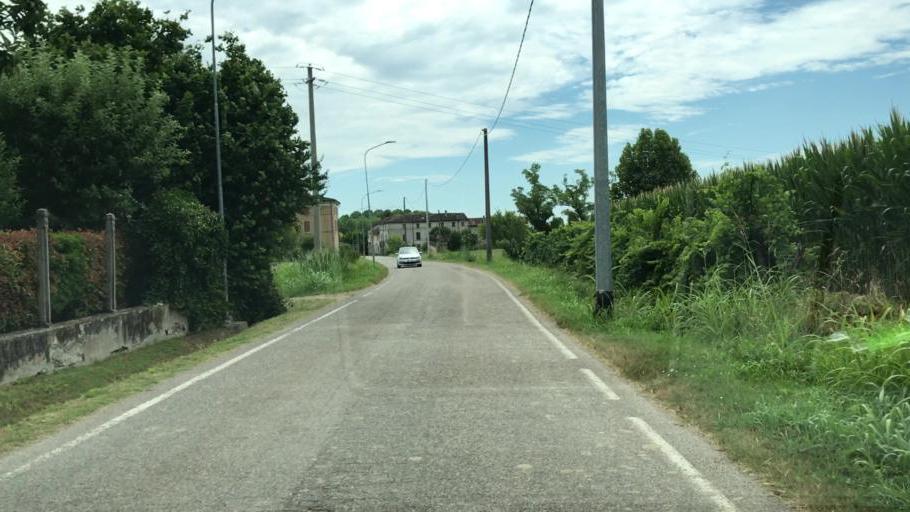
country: IT
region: Lombardy
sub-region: Provincia di Mantova
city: Ceresara
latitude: 45.2671
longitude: 10.5763
